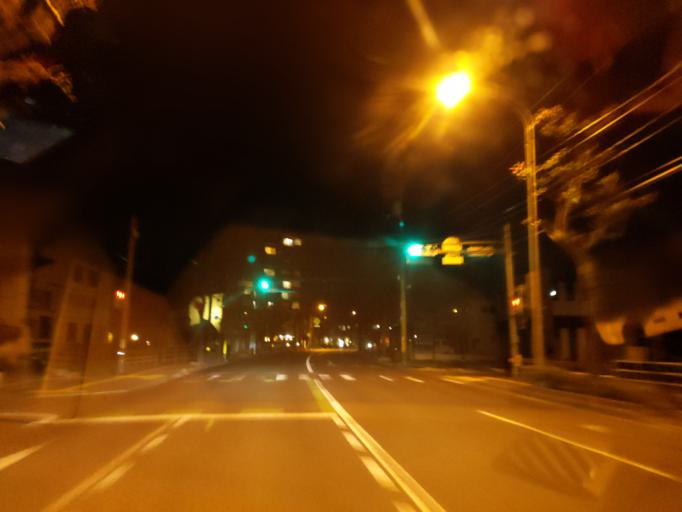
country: JP
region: Okayama
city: Okayama-shi
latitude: 34.6668
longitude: 133.9467
